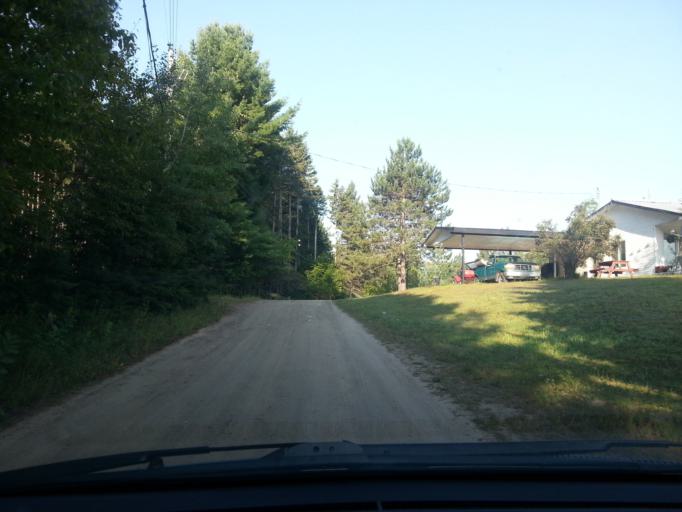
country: CA
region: Quebec
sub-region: Outaouais
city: Maniwaki
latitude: 46.2038
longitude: -76.1350
